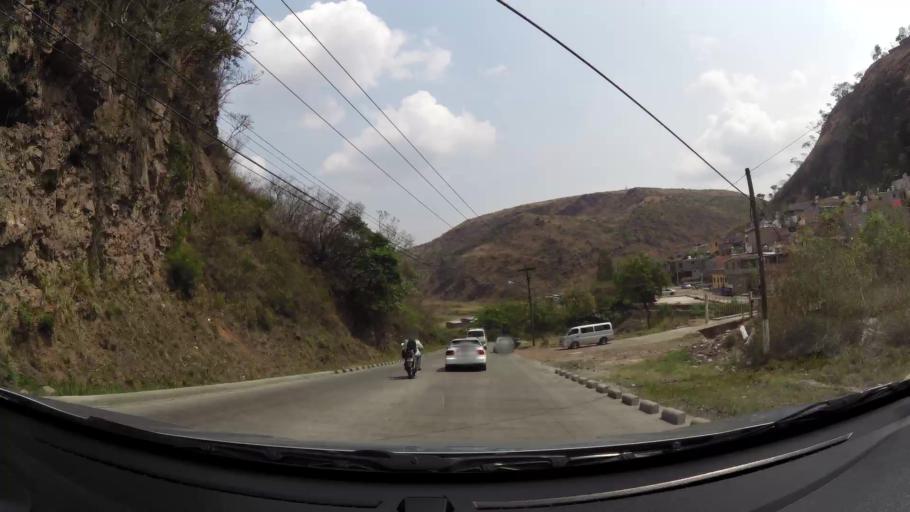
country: HN
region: Francisco Morazan
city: Tegucigalpa
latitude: 14.1183
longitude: -87.2179
